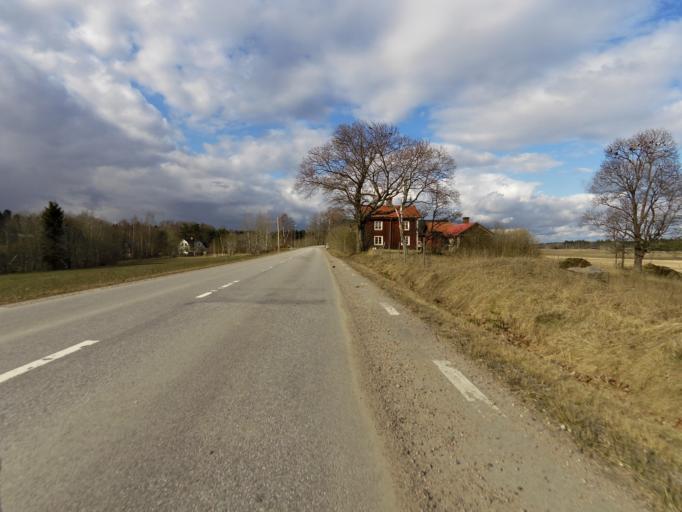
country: SE
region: Dalarna
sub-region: Avesta Kommun
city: Horndal
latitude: 60.4668
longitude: 16.4563
